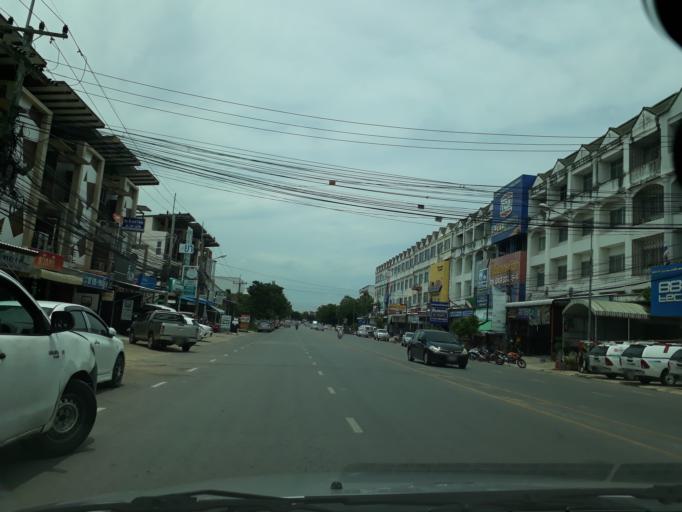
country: TH
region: Khon Kaen
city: Khon Kaen
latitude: 16.4339
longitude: 102.8625
